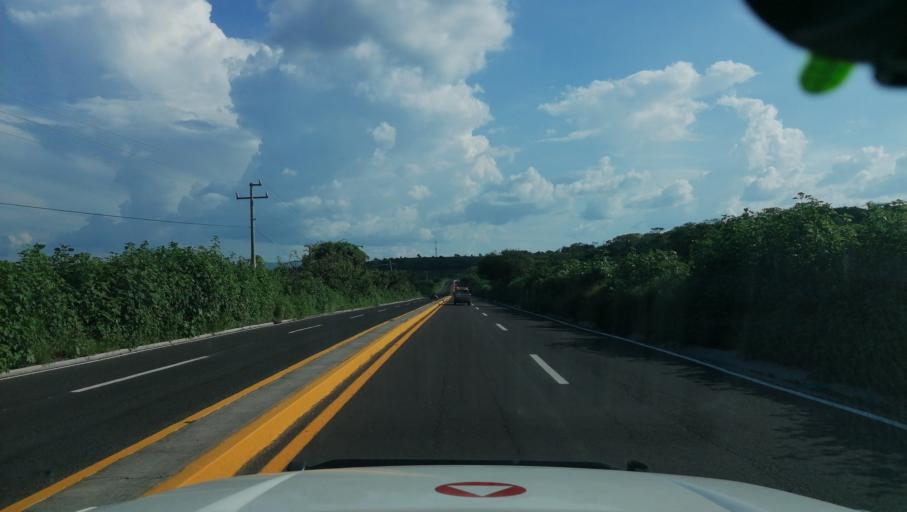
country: MX
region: Morelos
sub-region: Ayala
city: Abelardo L. Rodriguez
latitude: 18.7086
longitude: -98.9909
